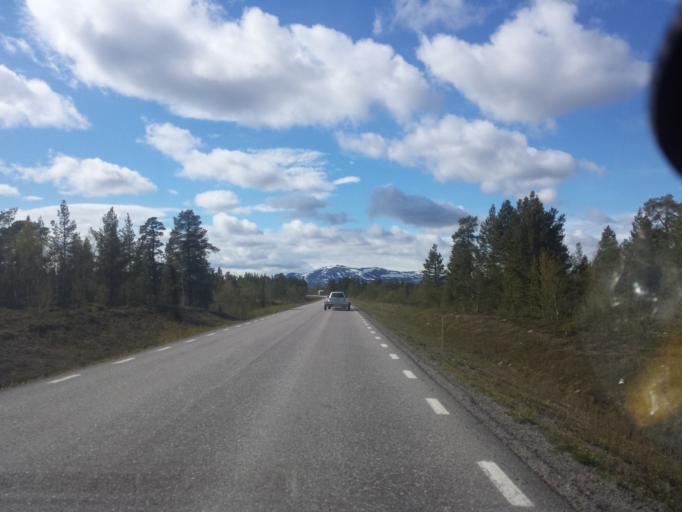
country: SE
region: Norrbotten
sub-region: Kiruna Kommun
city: Kiruna
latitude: 67.9930
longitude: 19.9119
